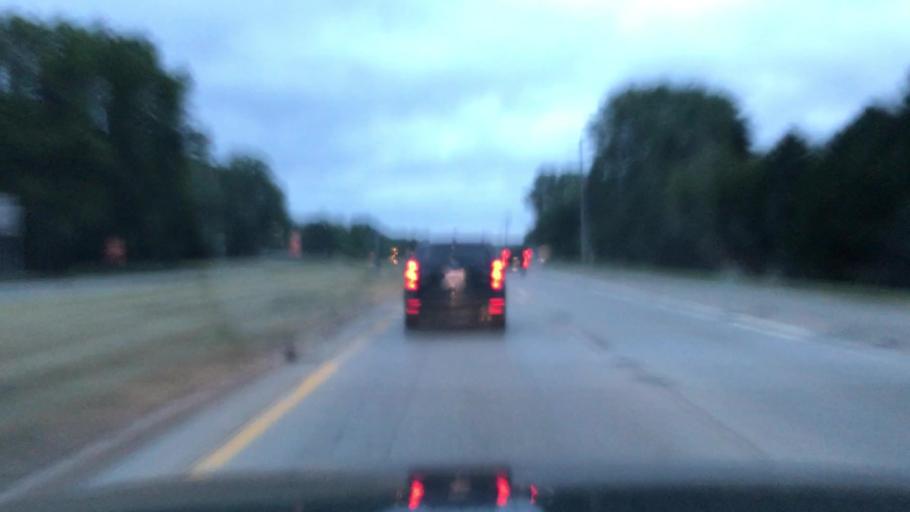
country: US
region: Michigan
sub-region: Kent County
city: East Grand Rapids
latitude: 42.9334
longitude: -85.5847
